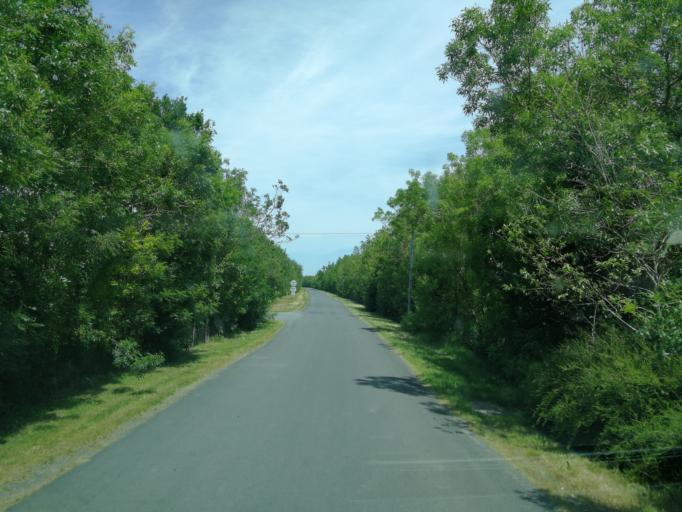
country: FR
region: Pays de la Loire
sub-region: Departement de la Vendee
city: Le Langon
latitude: 46.3977
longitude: -0.9315
